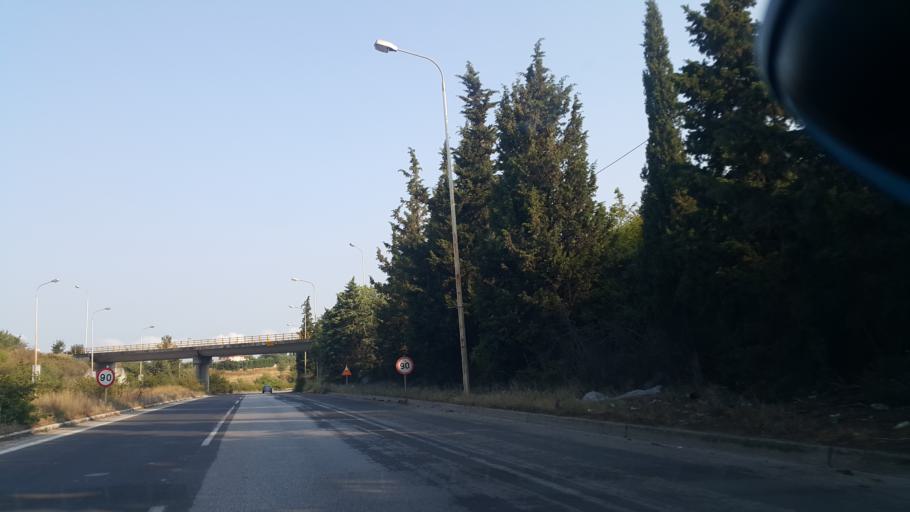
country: GR
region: Central Macedonia
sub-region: Nomos Thessalonikis
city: Kardia
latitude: 40.4581
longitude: 23.0016
